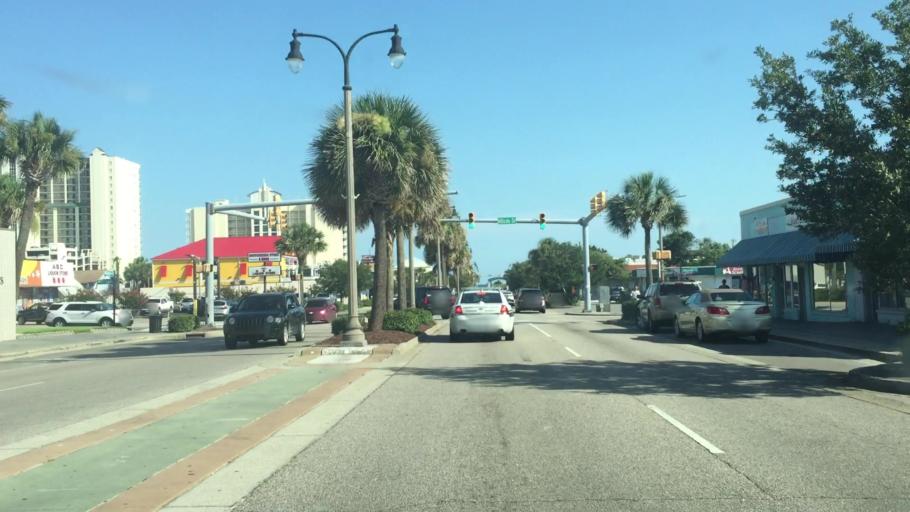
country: US
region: South Carolina
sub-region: Horry County
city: North Myrtle Beach
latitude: 33.8210
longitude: -78.6736
